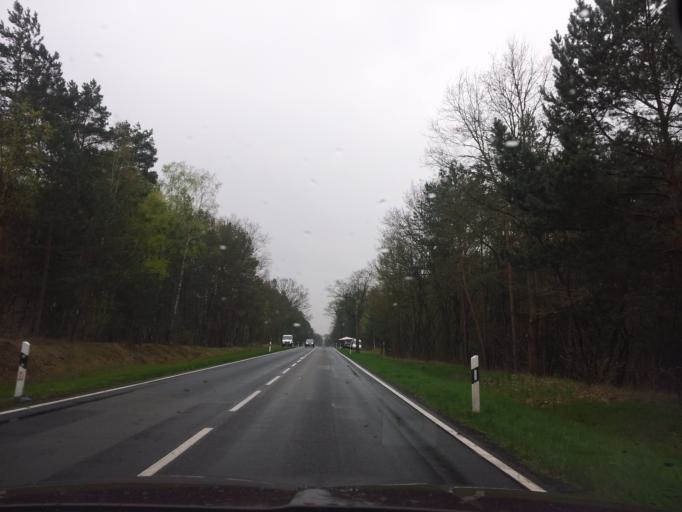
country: DE
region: Brandenburg
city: Treuenbrietzen
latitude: 52.0652
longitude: 12.8284
